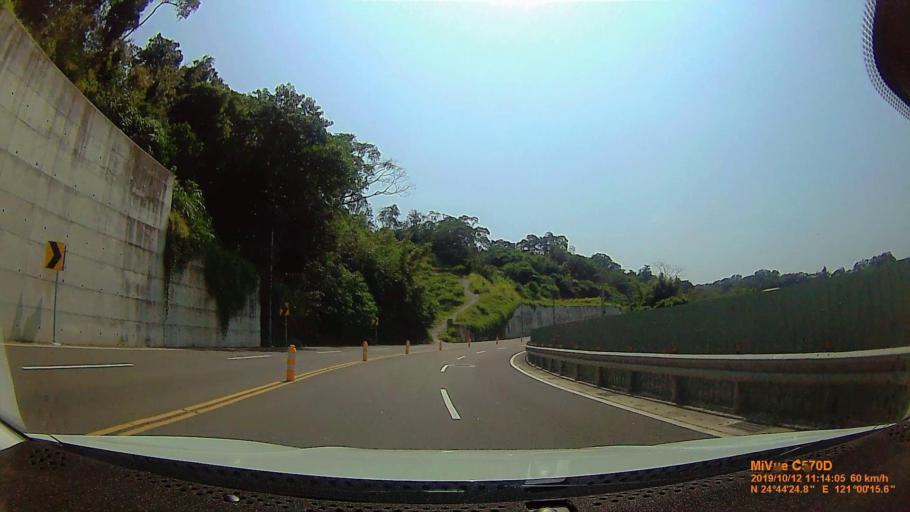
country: TW
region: Taiwan
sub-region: Hsinchu
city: Hsinchu
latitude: 24.7399
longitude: 121.0042
